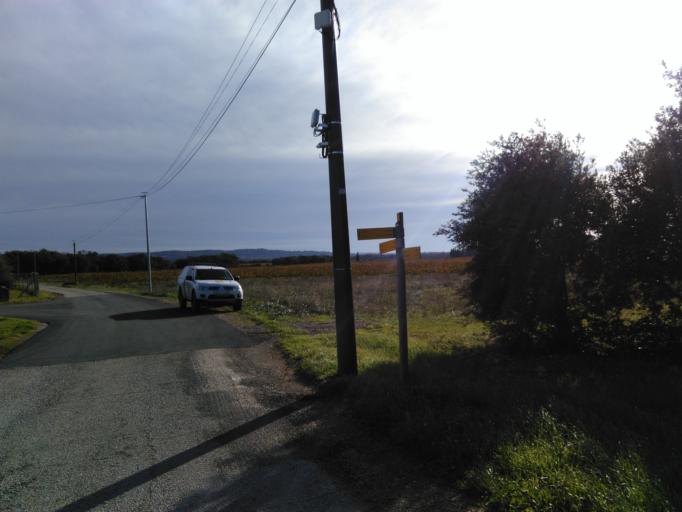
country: FR
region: Provence-Alpes-Cote d'Azur
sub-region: Departement du Vaucluse
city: Grillon
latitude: 44.3795
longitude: 4.9396
